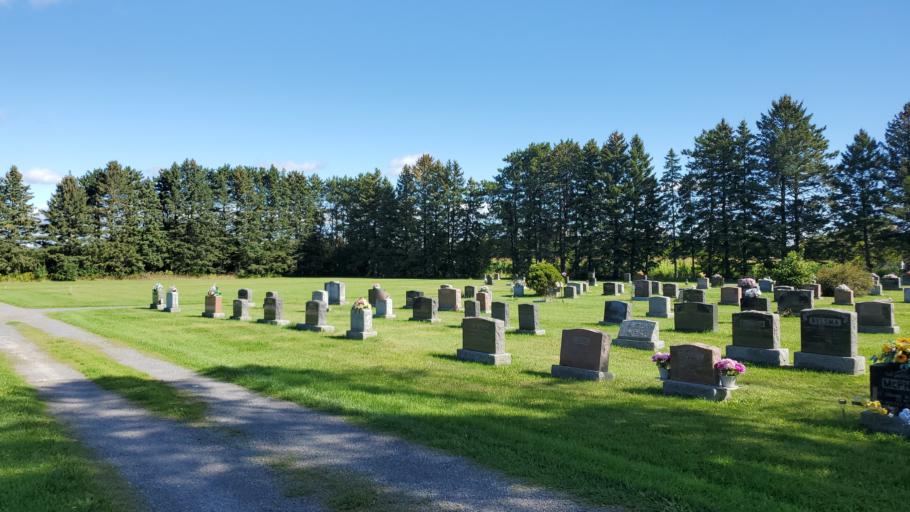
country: US
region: New York
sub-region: St. Lawrence County
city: Norfolk
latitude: 44.9731
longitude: -75.2566
